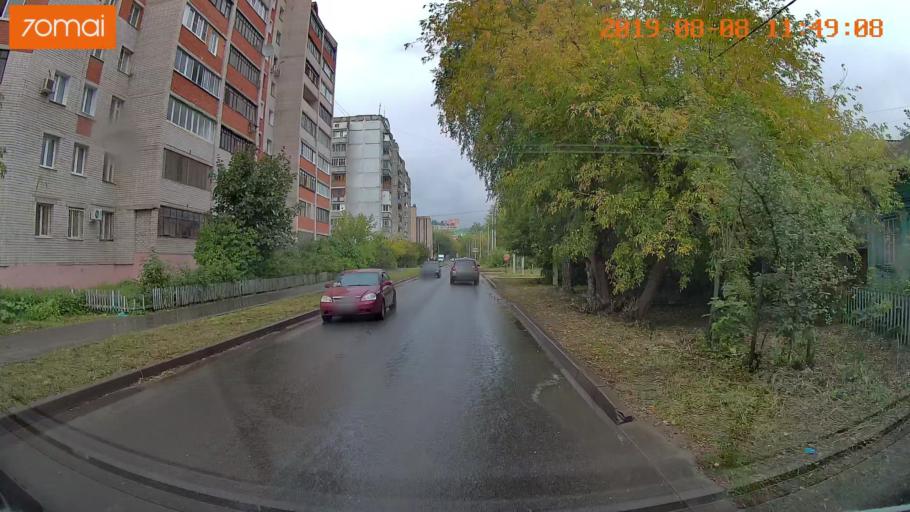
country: RU
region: Ivanovo
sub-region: Gorod Ivanovo
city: Ivanovo
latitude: 56.9758
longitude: 40.9831
